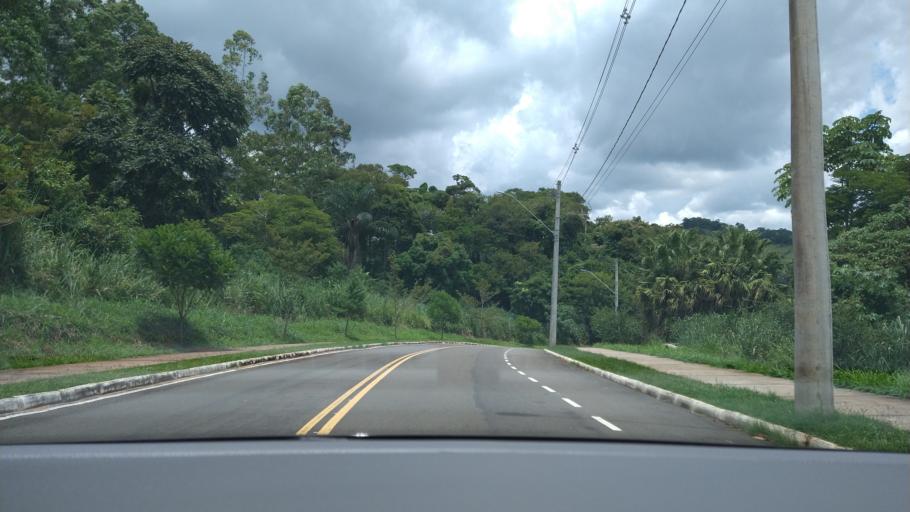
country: BR
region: Minas Gerais
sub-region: Vicosa
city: Vicosa
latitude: -20.7648
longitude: -42.8584
